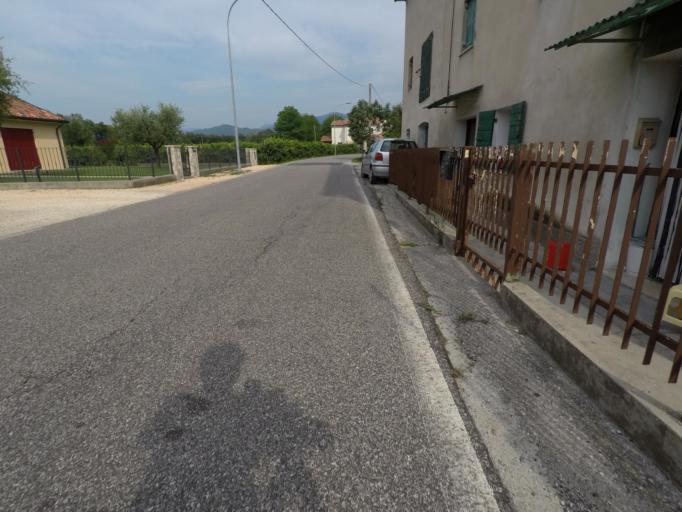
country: IT
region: Veneto
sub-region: Provincia di Treviso
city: Cappella Maggiore
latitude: 45.9673
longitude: 12.3441
